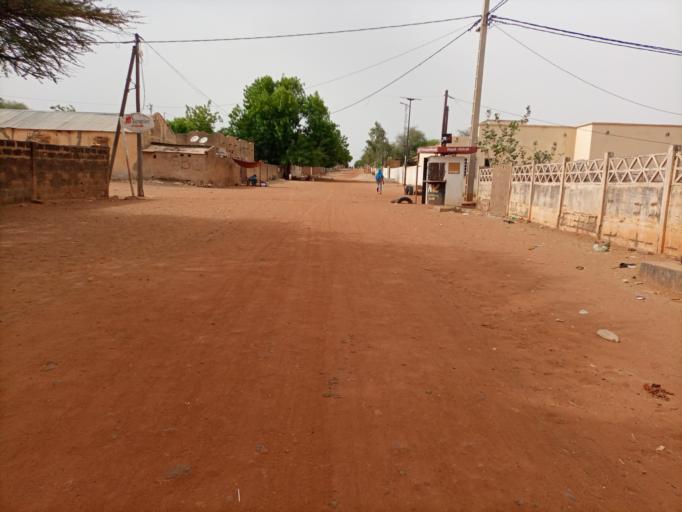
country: SN
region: Louga
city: Ndibene Dahra
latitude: 15.3971
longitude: -15.1170
